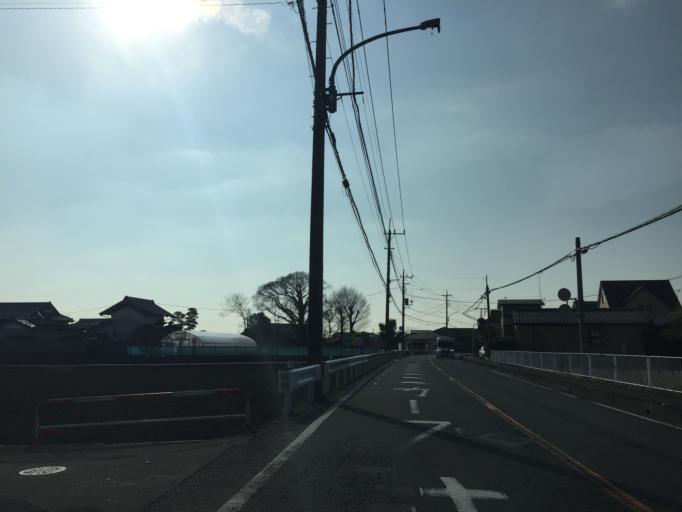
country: JP
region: Saitama
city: Kamifukuoka
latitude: 35.8786
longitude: 139.5527
